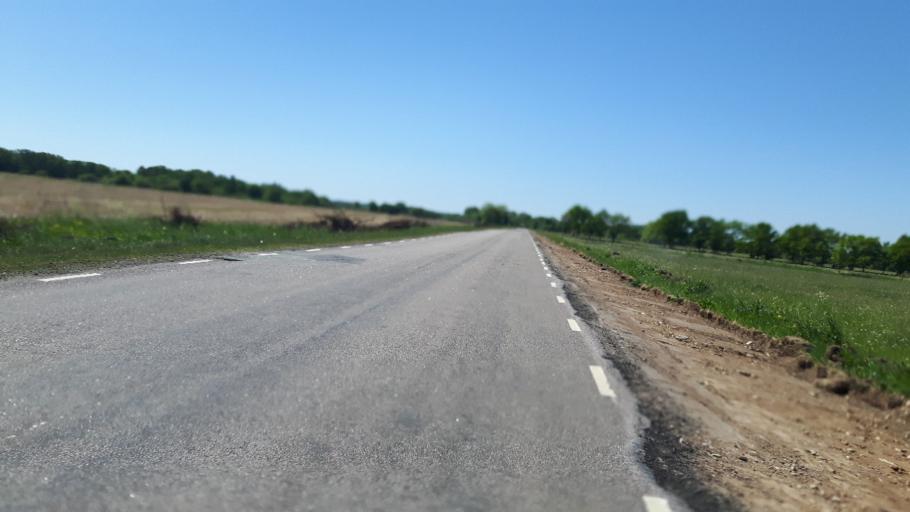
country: EE
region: Ida-Virumaa
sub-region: Narva-Joesuu linn
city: Narva-Joesuu
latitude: 59.3985
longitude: 27.9316
